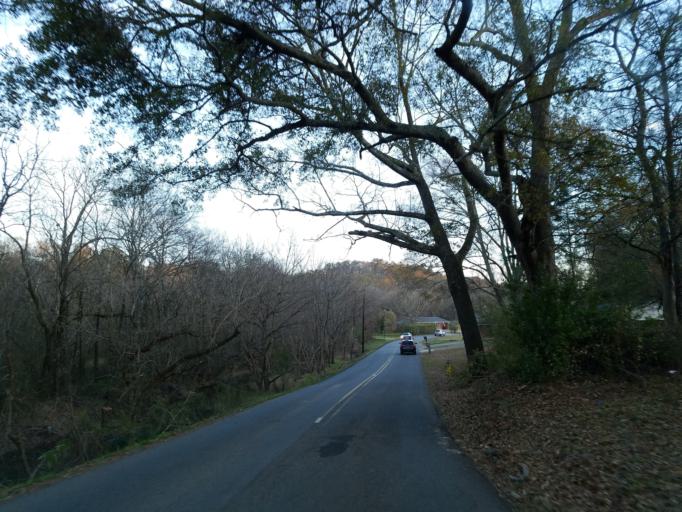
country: US
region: Georgia
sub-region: Bartow County
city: Cartersville
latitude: 34.1968
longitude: -84.8138
